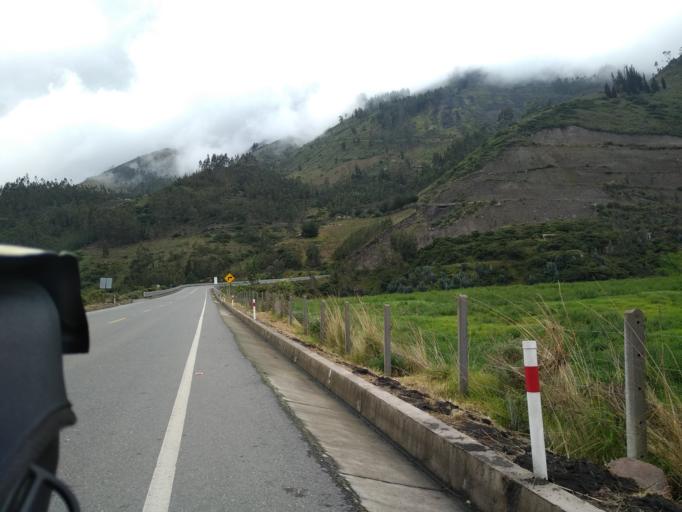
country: EC
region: Tungurahua
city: Banos
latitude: -1.5052
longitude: -78.5219
